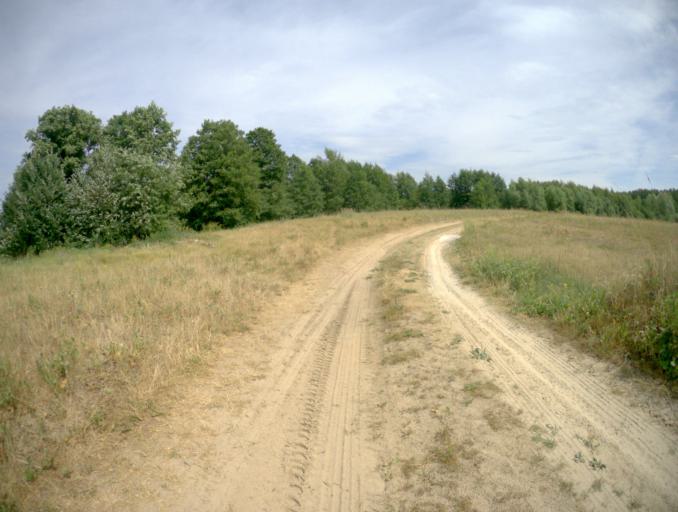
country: RU
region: Vladimir
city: Raduzhnyy
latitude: 56.0292
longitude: 40.3171
